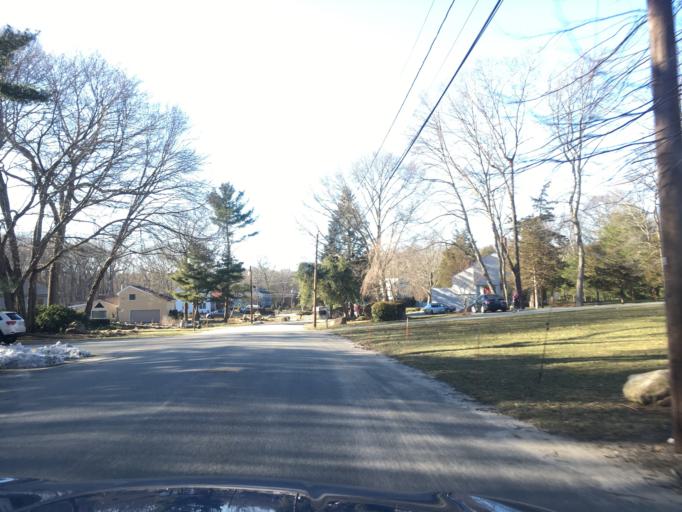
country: US
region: Rhode Island
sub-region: Kent County
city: East Greenwich
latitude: 41.6492
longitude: -71.4909
